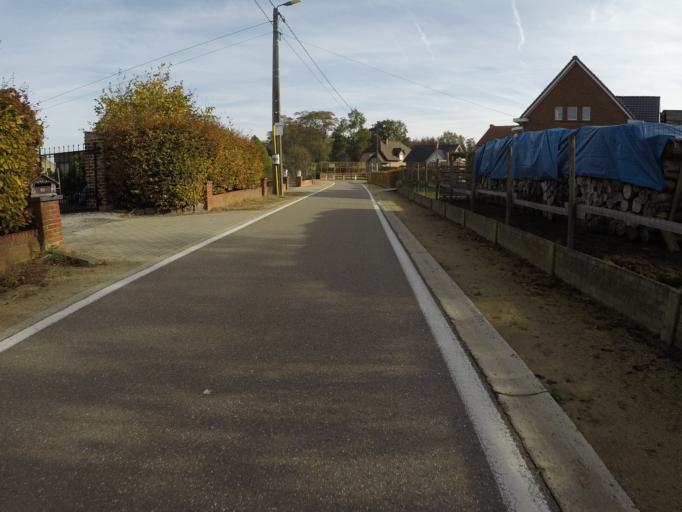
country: BE
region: Flanders
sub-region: Provincie Vlaams-Brabant
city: Begijnendijk
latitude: 50.9920
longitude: 4.7997
